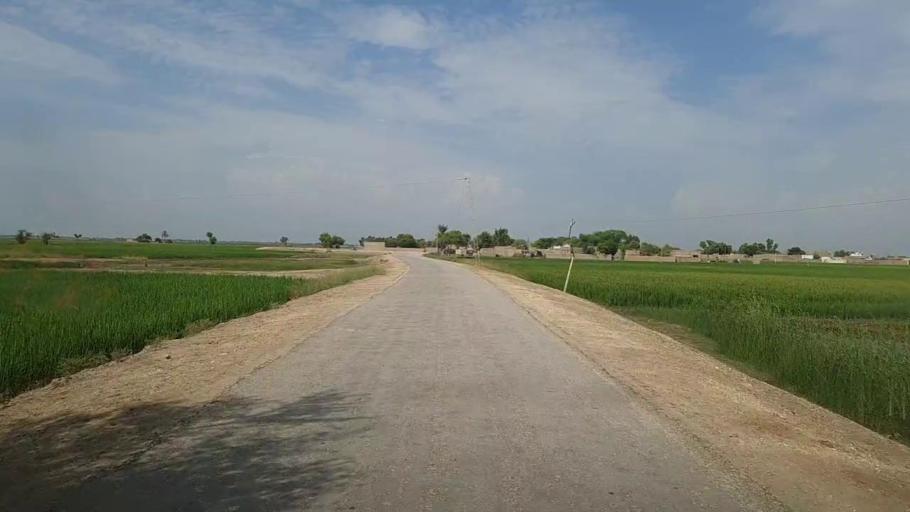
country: PK
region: Sindh
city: Thul
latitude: 28.2652
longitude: 68.8174
